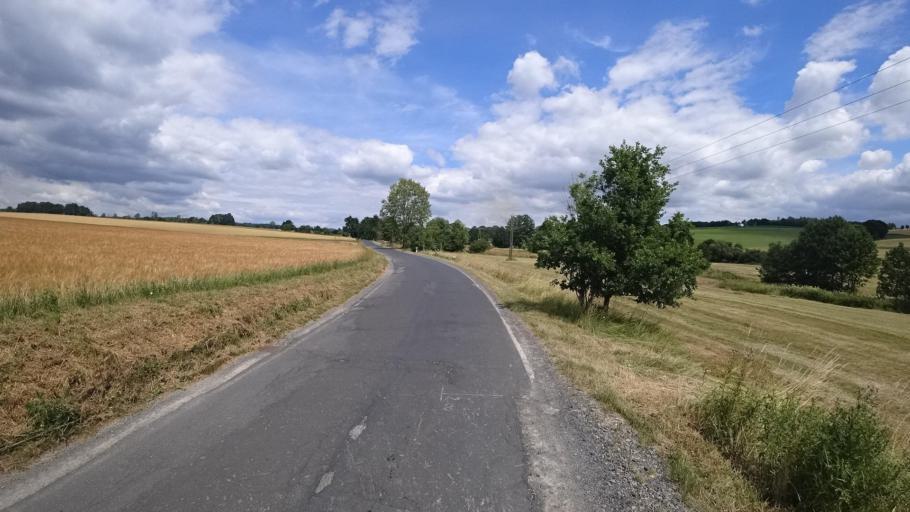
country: DE
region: Rheinland-Pfalz
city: Forstmehren
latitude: 50.7043
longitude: 7.5315
